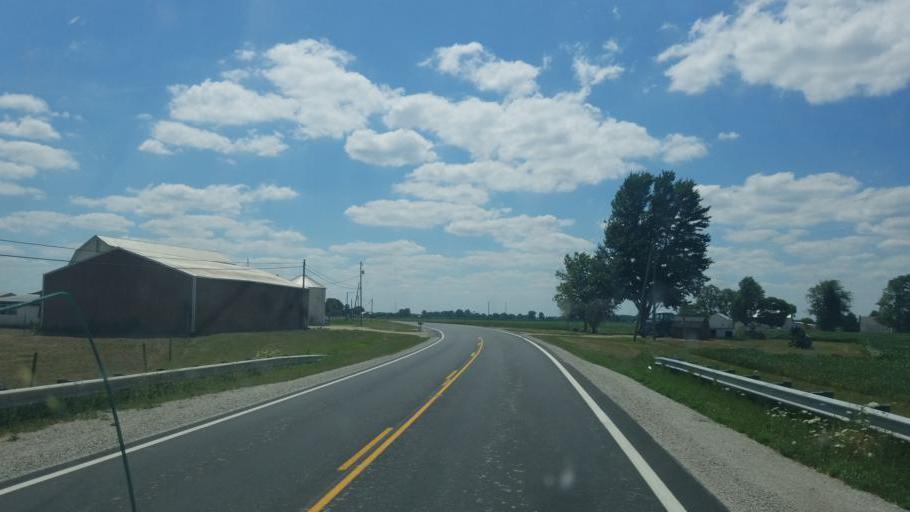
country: US
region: Ohio
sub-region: Defiance County
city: Hicksville
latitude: 41.3170
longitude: -84.7252
